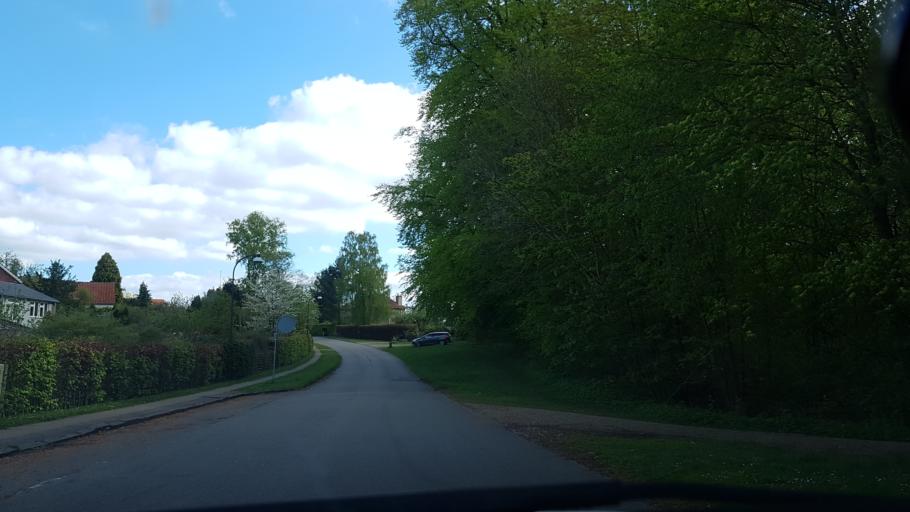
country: DK
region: Capital Region
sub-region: Rudersdal Kommune
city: Holte
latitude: 55.8201
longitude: 12.4587
